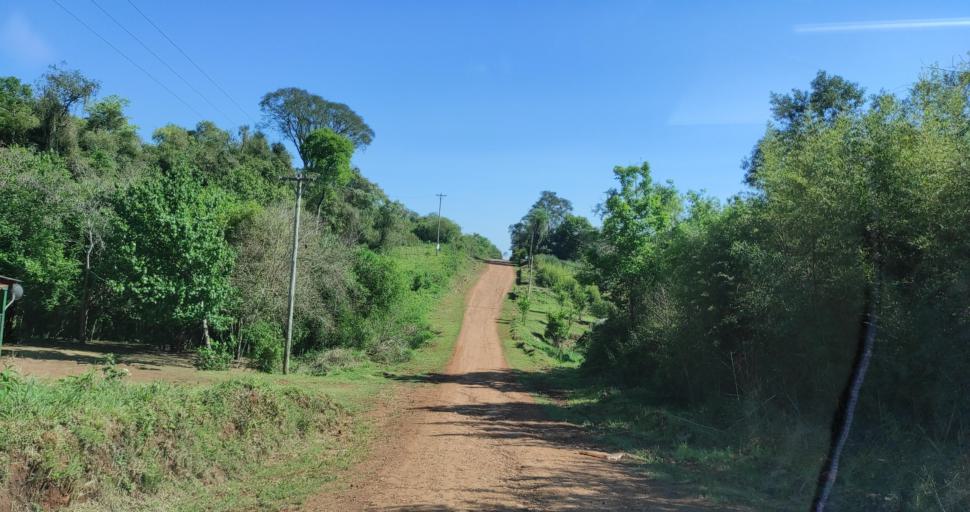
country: AR
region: Misiones
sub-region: Departamento de Candelaria
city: Loreto
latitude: -27.3185
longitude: -55.5330
